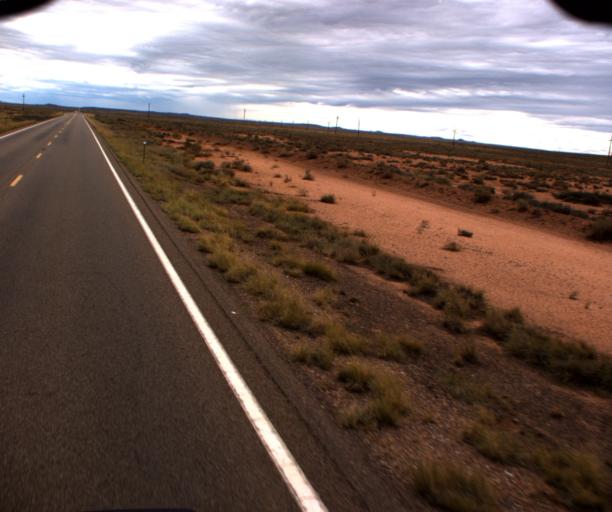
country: US
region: Arizona
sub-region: Navajo County
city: Holbrook
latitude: 34.8029
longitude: -110.1360
